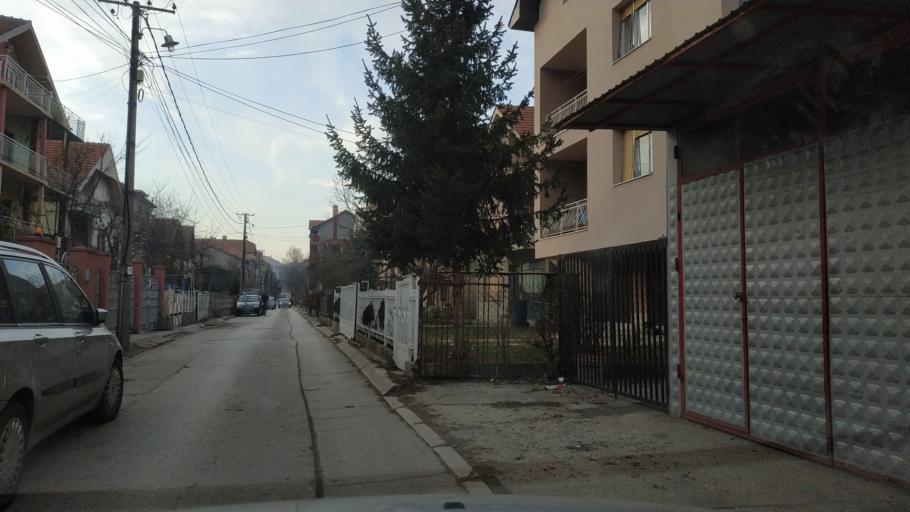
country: RS
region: Central Serbia
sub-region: Nisavski Okrug
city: Nis
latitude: 43.3187
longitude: 21.9320
